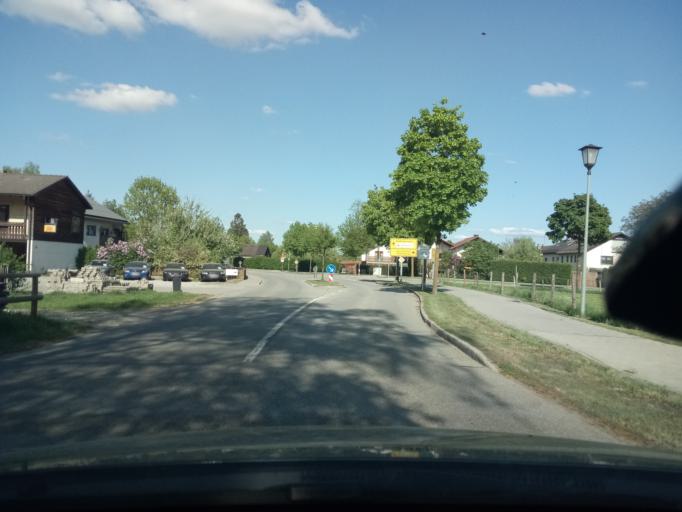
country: DE
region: Bavaria
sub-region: Upper Bavaria
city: Aschau am Inn
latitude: 48.1968
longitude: 12.3479
